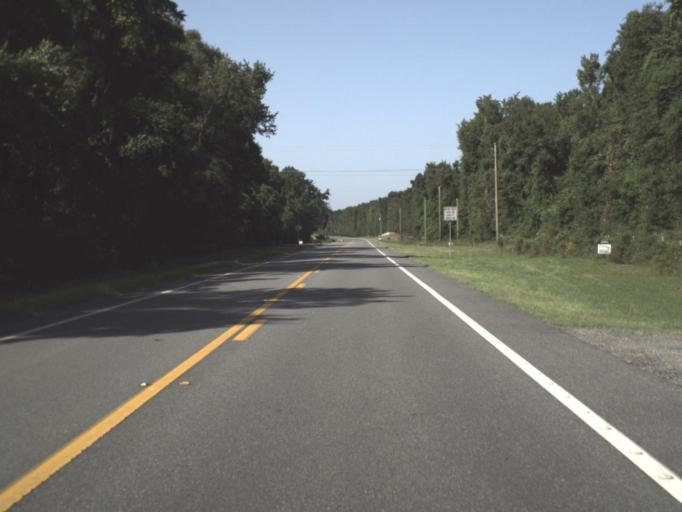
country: US
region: Florida
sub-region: Alachua County
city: High Springs
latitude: 29.9119
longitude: -82.7174
